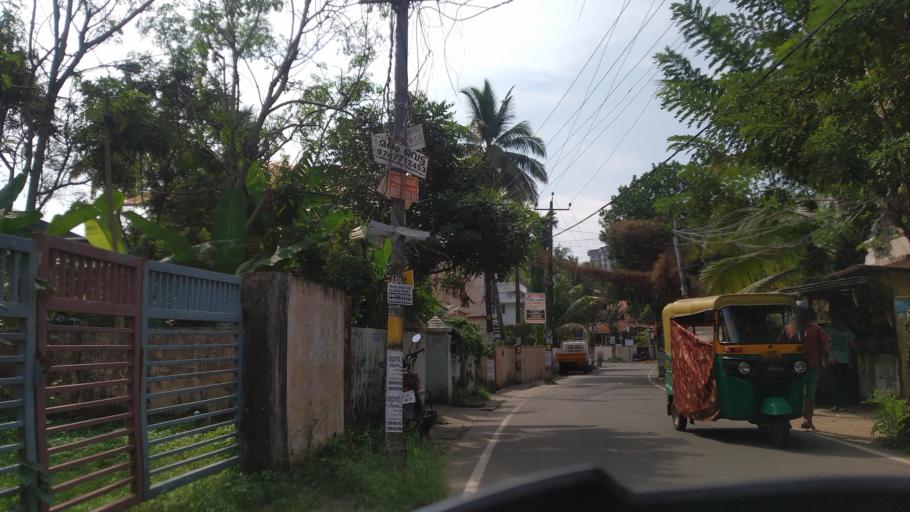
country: IN
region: Kerala
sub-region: Ernakulam
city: Elur
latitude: 10.0086
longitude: 76.3006
